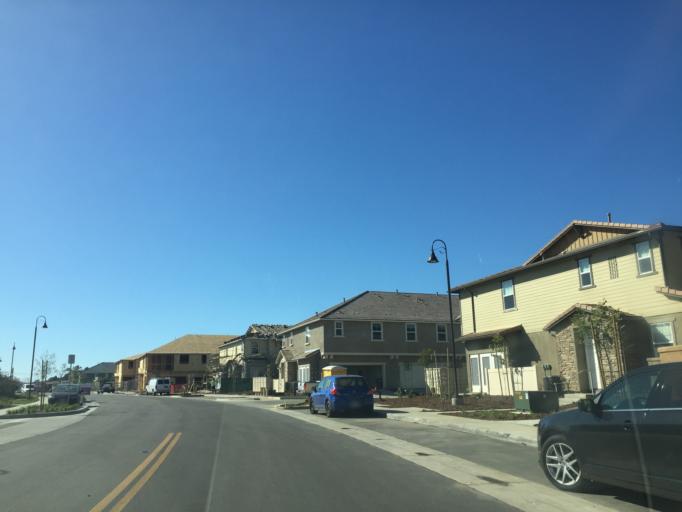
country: US
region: California
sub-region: Santa Barbara County
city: Isla Vista
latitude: 34.4358
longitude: -119.8550
